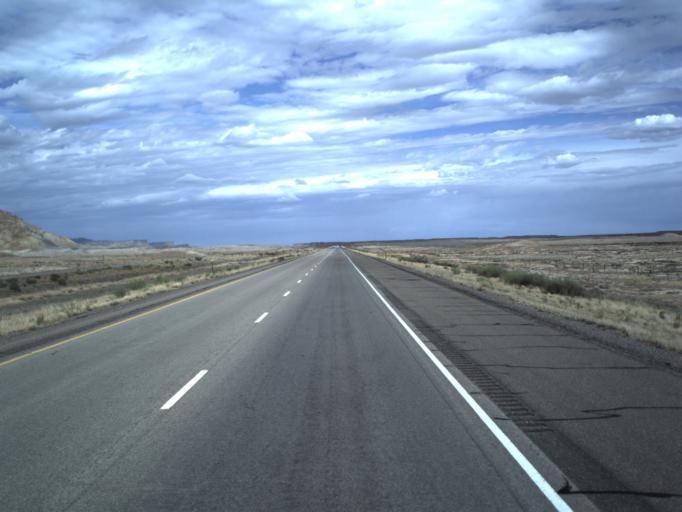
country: US
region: Utah
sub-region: Grand County
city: Moab
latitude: 38.9273
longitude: -109.8940
